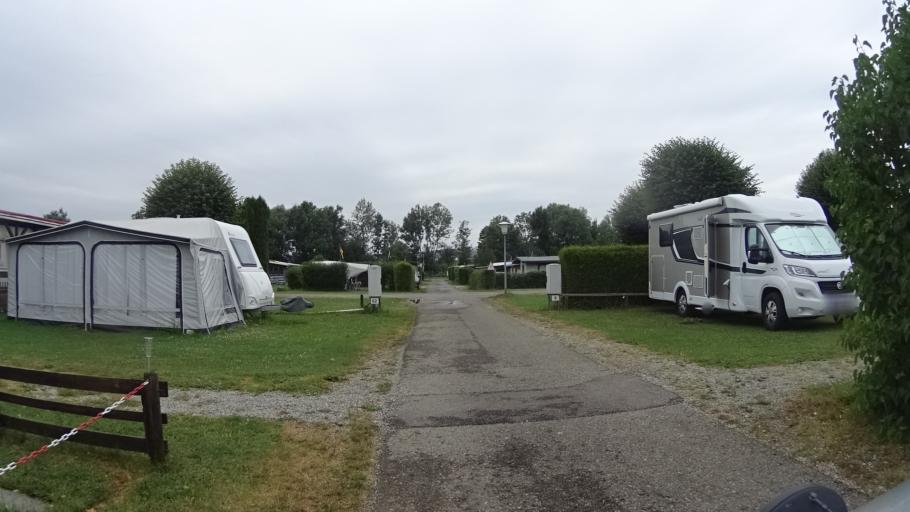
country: DE
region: Baden-Wuerttemberg
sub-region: Tuebingen Region
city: Kirchberg an der Iller
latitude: 48.1382
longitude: 10.1039
